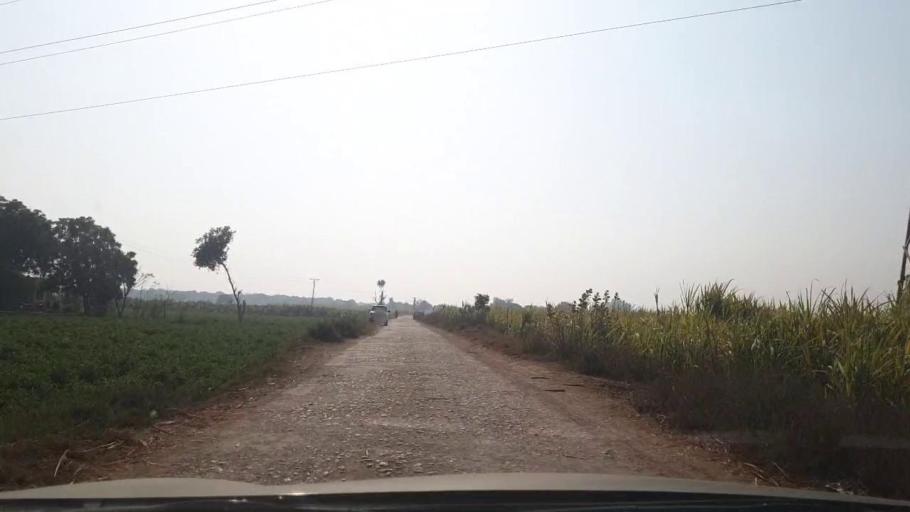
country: PK
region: Sindh
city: Tando Allahyar
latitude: 25.4935
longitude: 68.7543
